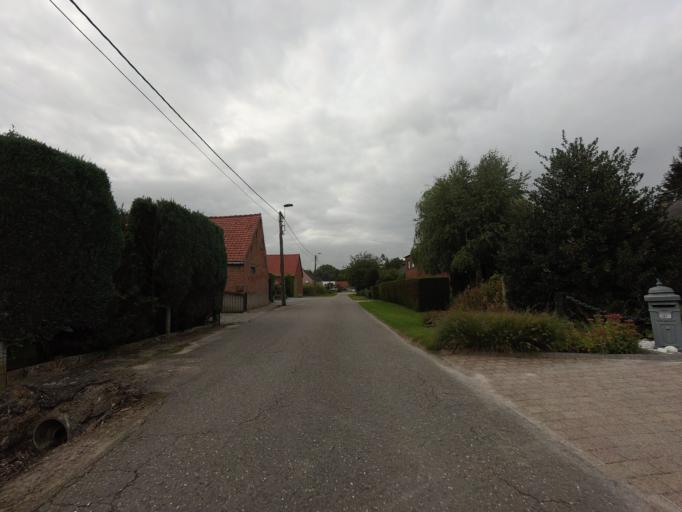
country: BE
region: Flanders
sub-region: Provincie Vlaams-Brabant
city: Londerzeel
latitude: 50.9759
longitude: 4.3191
